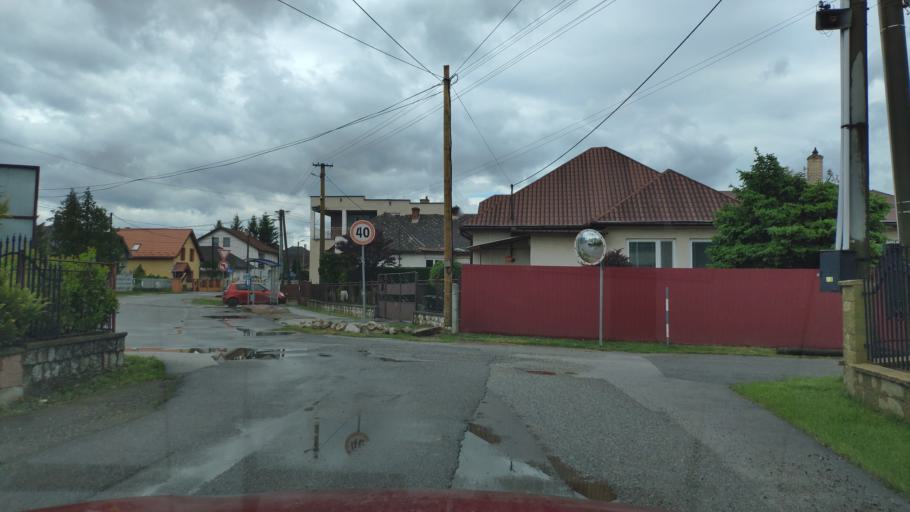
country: SK
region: Kosicky
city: Moldava nad Bodvou
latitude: 48.5730
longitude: 21.1216
